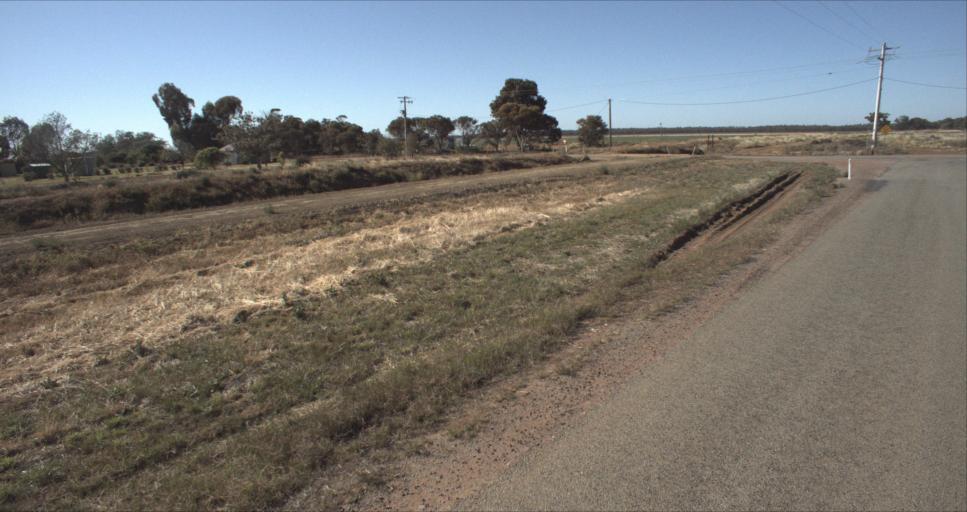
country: AU
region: New South Wales
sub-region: Leeton
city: Leeton
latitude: -34.5829
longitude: 146.3084
